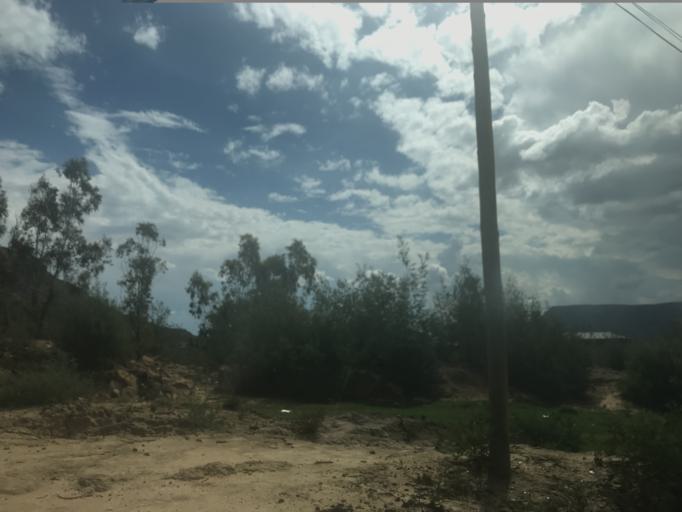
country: LS
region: Maseru
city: Nako
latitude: -29.6297
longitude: 27.5133
